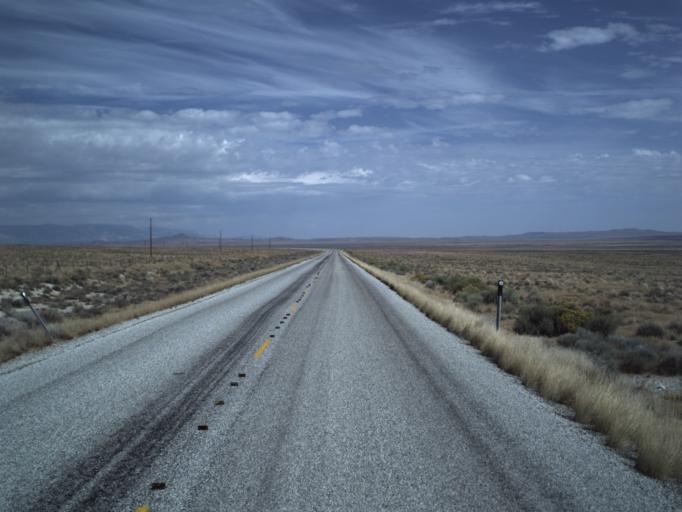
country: US
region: Utah
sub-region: Tooele County
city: Wendover
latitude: 41.4996
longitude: -113.6089
